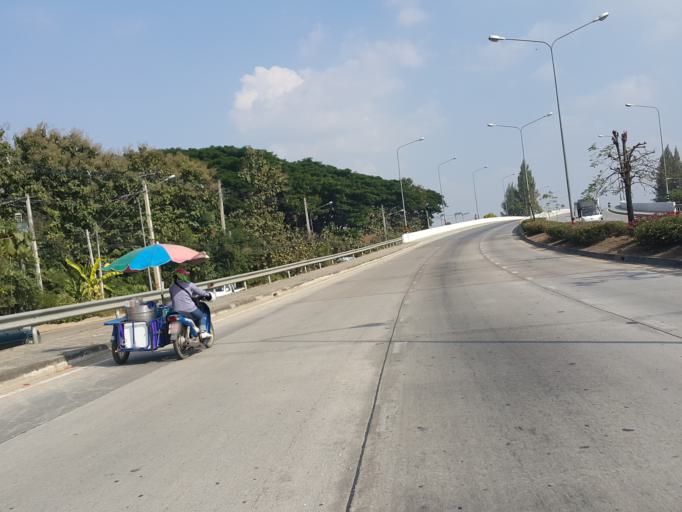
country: TH
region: Chiang Mai
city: Chiang Mai
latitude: 18.7463
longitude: 98.9822
